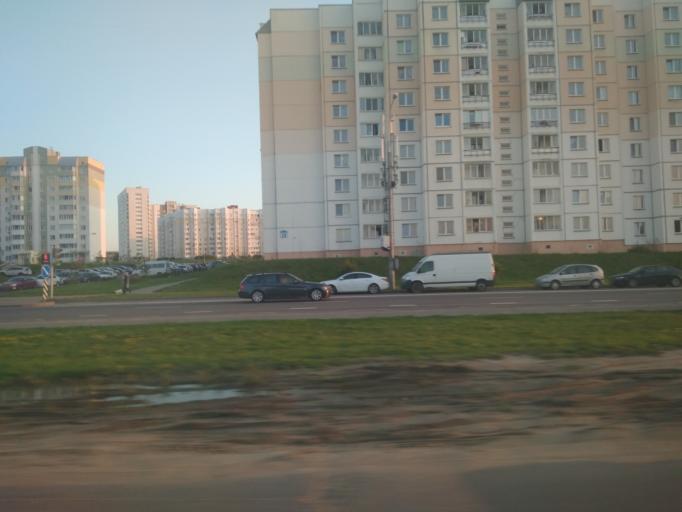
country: BY
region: Minsk
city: Novoye Medvezhino
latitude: 53.9208
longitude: 27.4633
